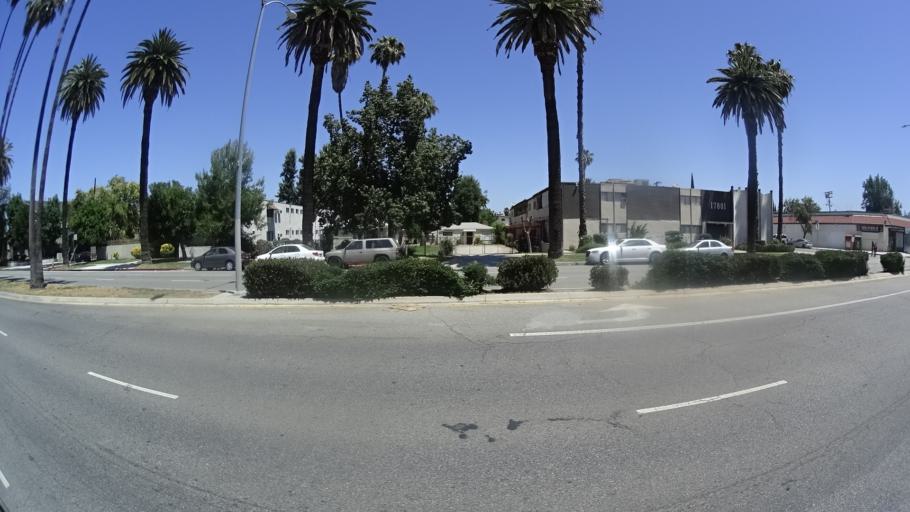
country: US
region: California
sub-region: Los Angeles County
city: Northridge
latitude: 34.2012
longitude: -118.5213
